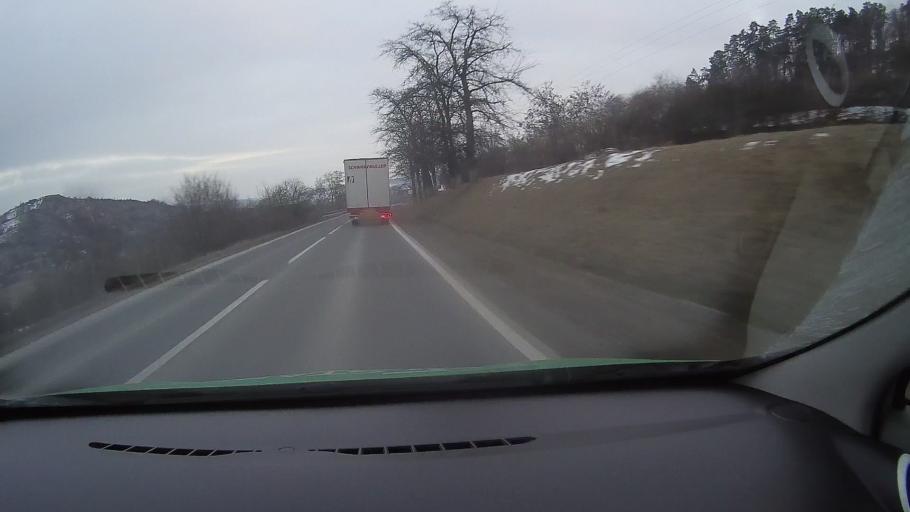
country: RO
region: Harghita
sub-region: Municipiul Odorheiu Secuiesc
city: Odorheiu Secuiesc
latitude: 46.3259
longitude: 25.2789
